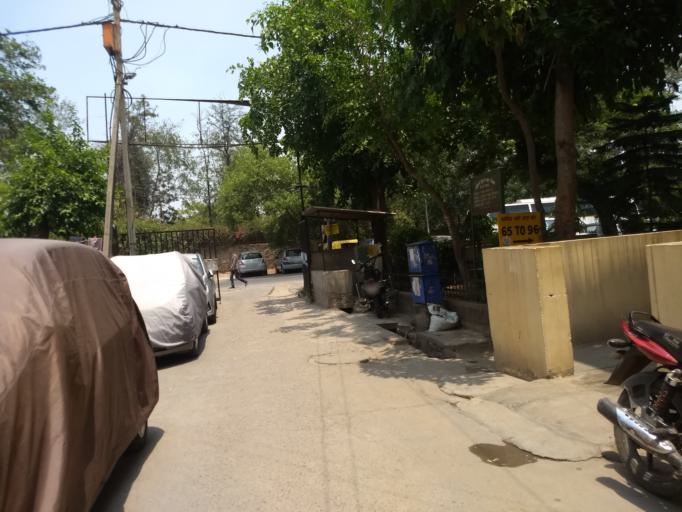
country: IN
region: NCT
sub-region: New Delhi
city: New Delhi
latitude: 28.5264
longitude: 77.1960
